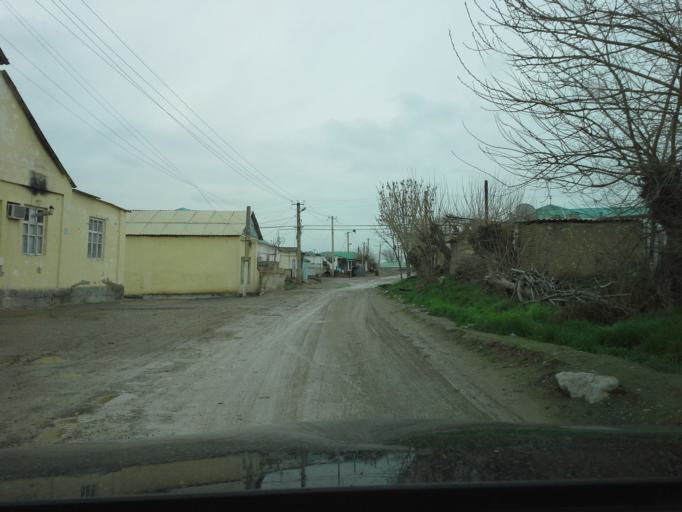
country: TM
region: Ahal
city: Abadan
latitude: 37.9603
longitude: 58.2075
